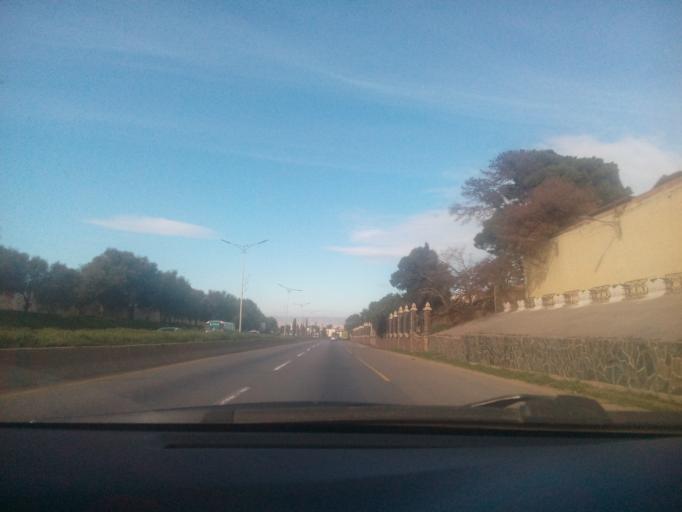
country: DZ
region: Oran
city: Es Senia
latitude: 35.6116
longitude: -0.5806
